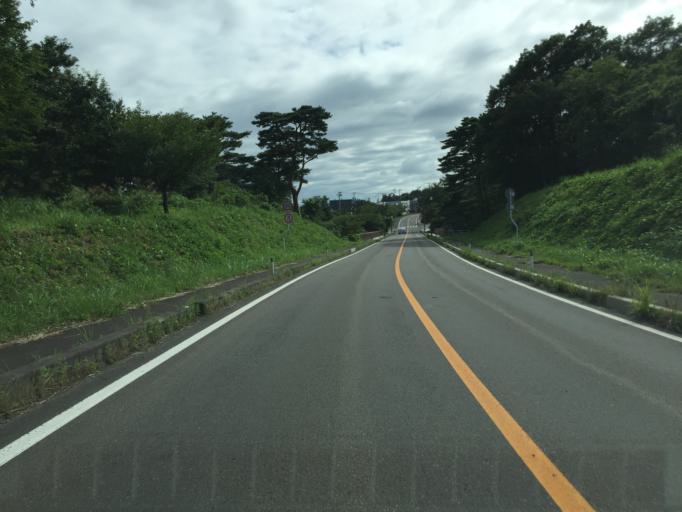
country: JP
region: Fukushima
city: Nihommatsu
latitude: 37.6082
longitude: 140.3593
